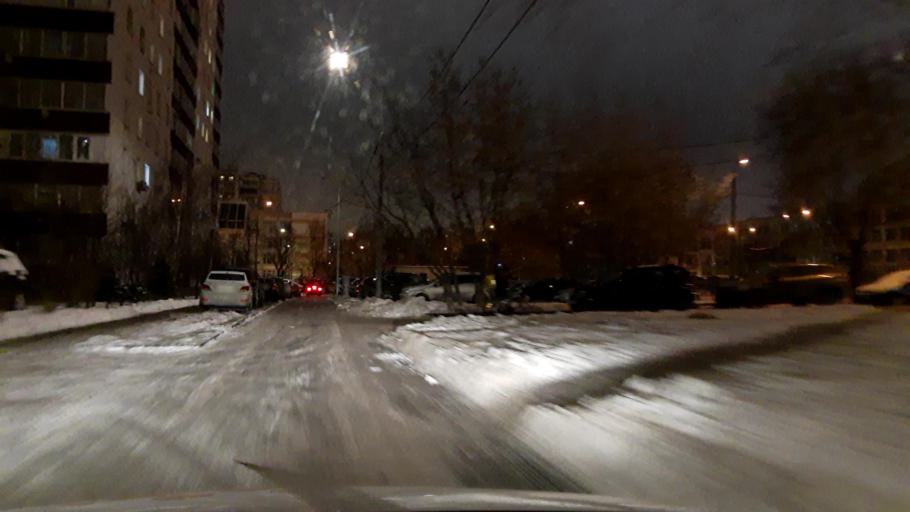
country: RU
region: Moscow
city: Lyublino
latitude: 55.6704
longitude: 37.7671
